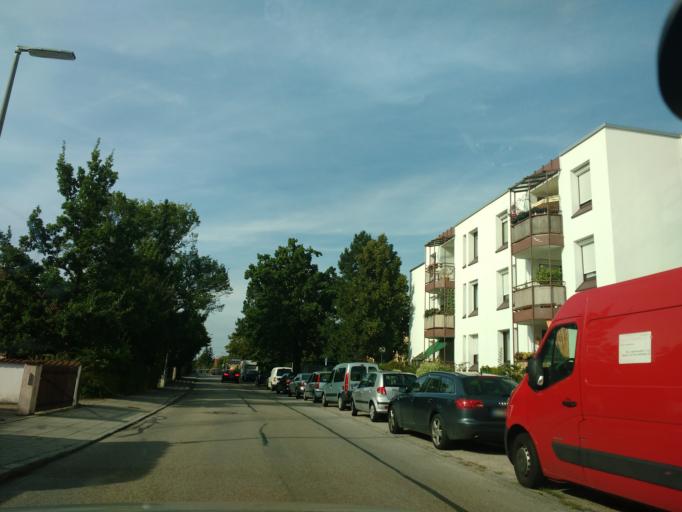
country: DE
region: Bavaria
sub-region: Upper Bavaria
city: Pasing
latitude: 48.1524
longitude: 11.4358
